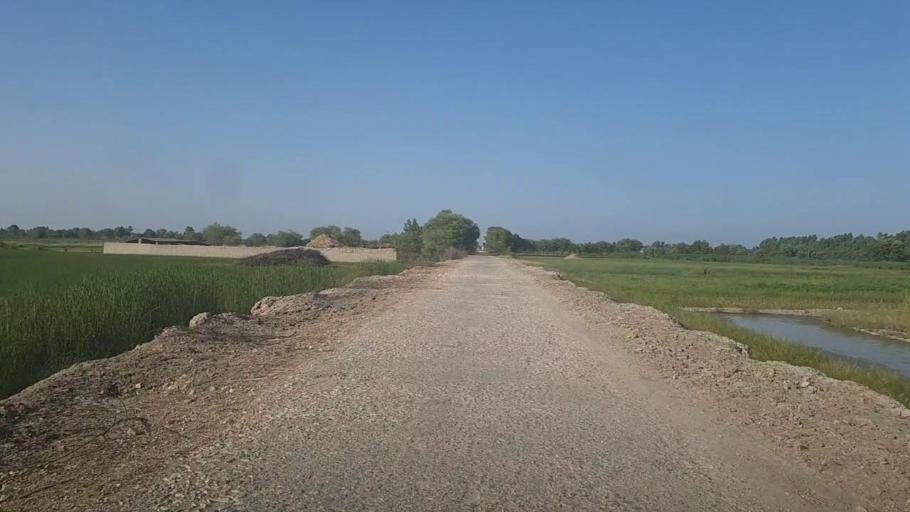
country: PK
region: Sindh
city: Khairpur
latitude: 28.1034
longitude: 69.6317
